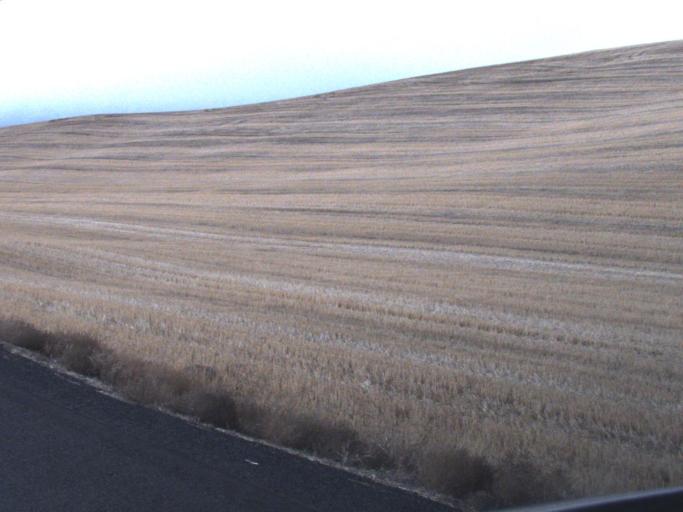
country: US
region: Washington
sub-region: Whitman County
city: Colfax
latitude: 46.8588
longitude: -117.4572
